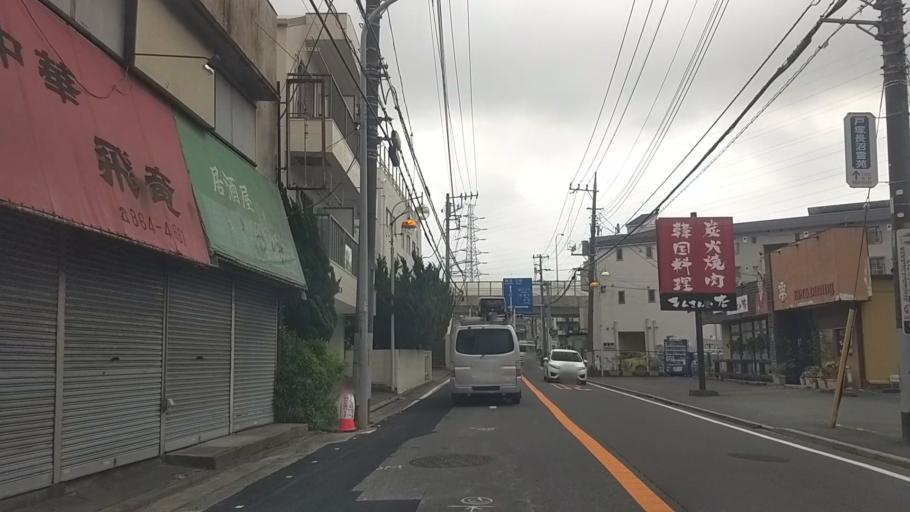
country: JP
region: Kanagawa
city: Kamakura
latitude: 35.3806
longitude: 139.5372
